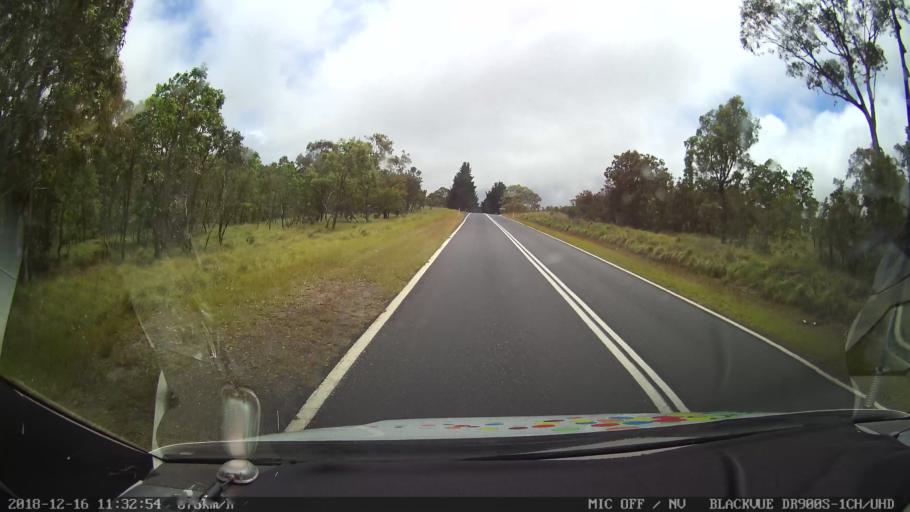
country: AU
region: New South Wales
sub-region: Tenterfield Municipality
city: Carrolls Creek
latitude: -29.0117
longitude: 152.1402
